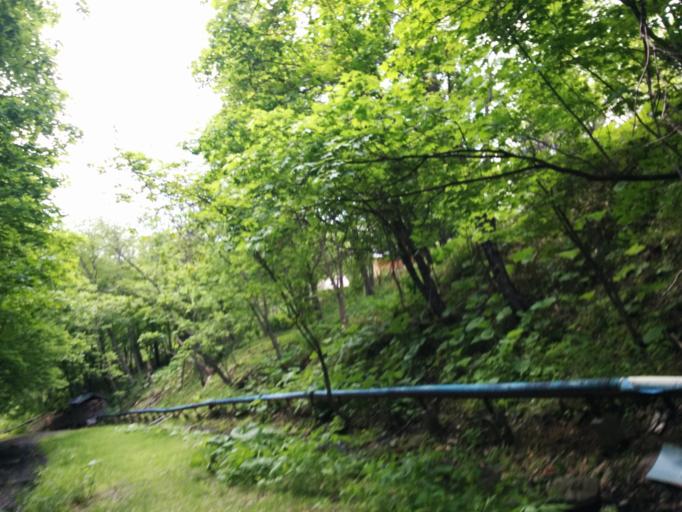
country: JP
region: Hokkaido
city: Otofuke
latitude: 43.3665
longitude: 143.1937
